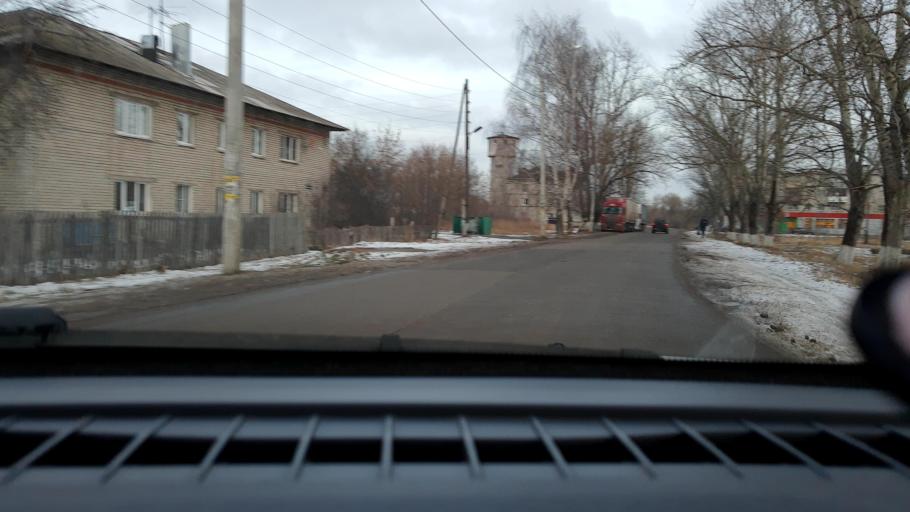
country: RU
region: Nizjnij Novgorod
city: Gorbatovka
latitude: 56.2487
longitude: 43.7474
